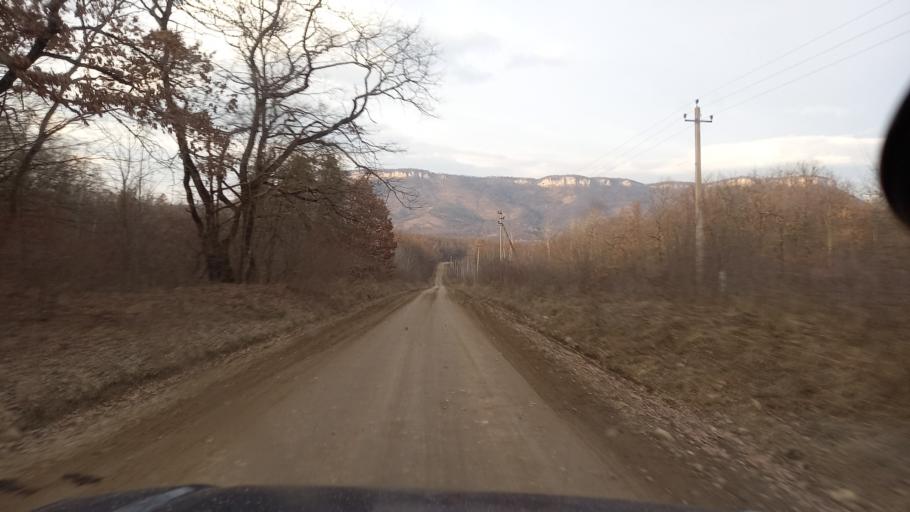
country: RU
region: Adygeya
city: Kamennomostskiy
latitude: 44.1983
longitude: 40.2519
